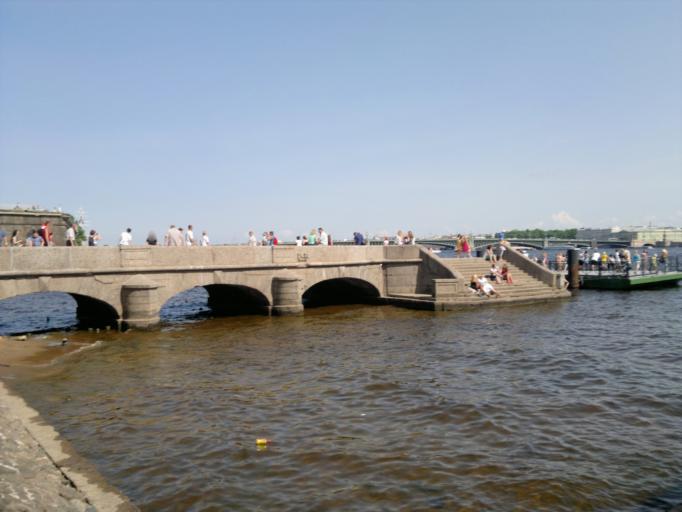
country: RU
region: St.-Petersburg
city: Saint Petersburg
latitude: 59.9491
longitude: 30.3182
